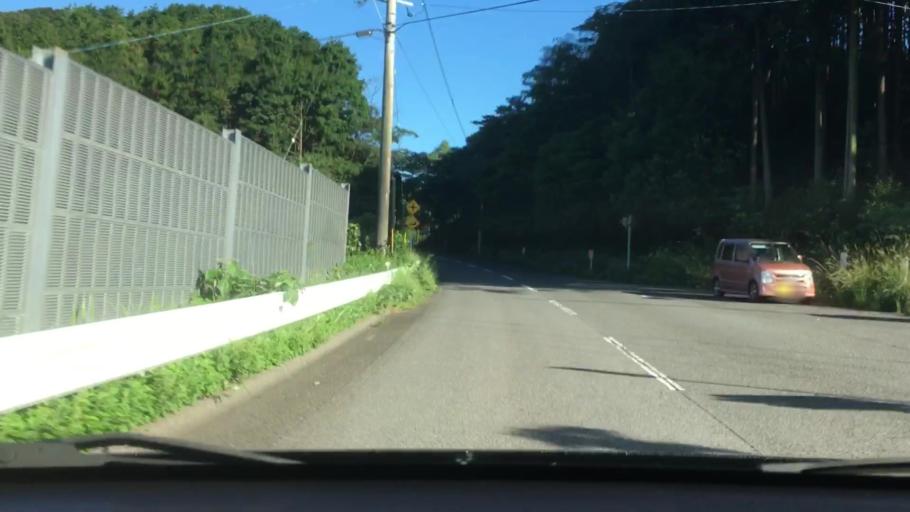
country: JP
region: Nagasaki
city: Sasebo
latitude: 33.0077
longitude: 129.7074
